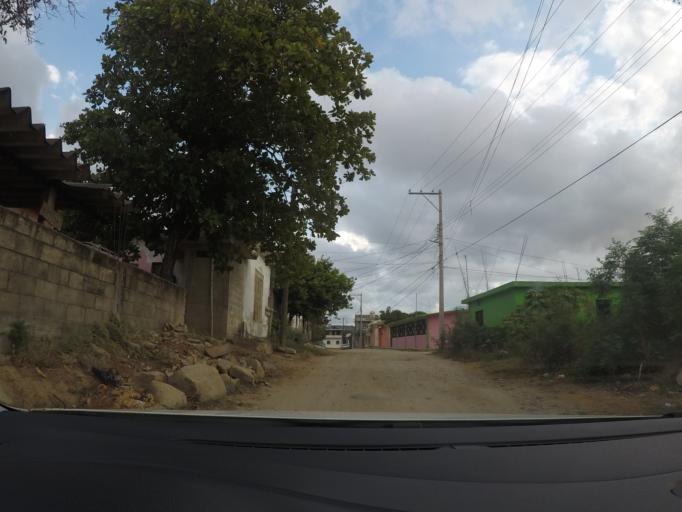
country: MX
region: Oaxaca
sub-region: Salina Cruz
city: Salina Cruz
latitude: 16.2126
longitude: -95.1989
